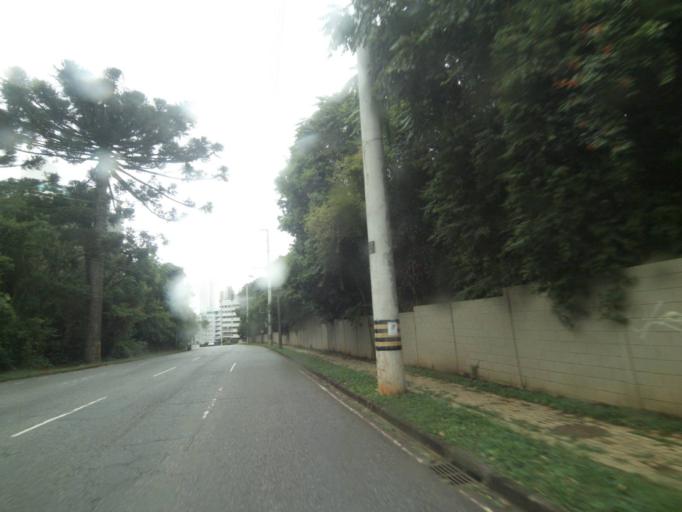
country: BR
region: Parana
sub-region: Curitiba
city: Curitiba
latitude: -25.4394
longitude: -49.3324
